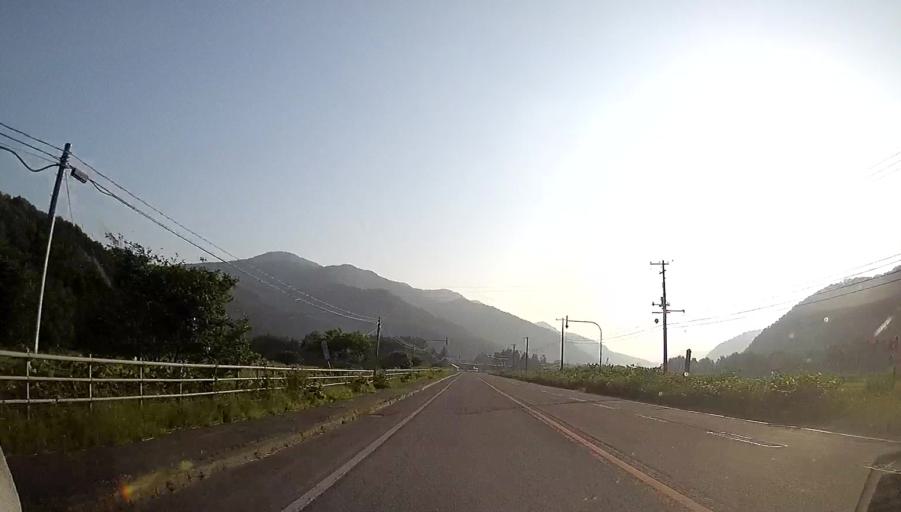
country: JP
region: Hokkaido
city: Shimo-furano
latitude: 42.8924
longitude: 142.5441
